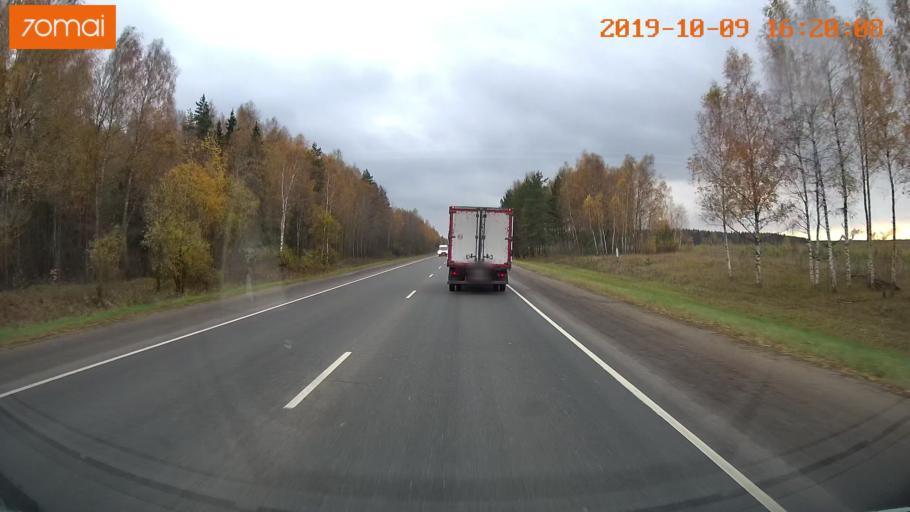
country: RU
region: Kostroma
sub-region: Kostromskoy Rayon
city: Kostroma
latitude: 57.7104
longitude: 40.8929
